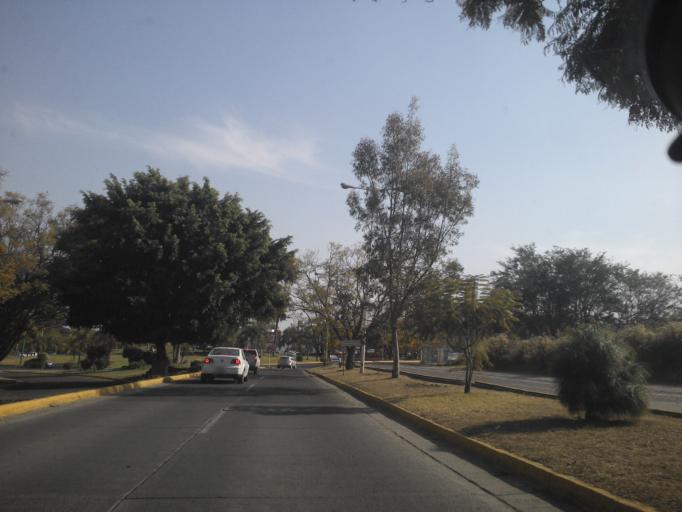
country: MX
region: Jalisco
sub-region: Tlajomulco de Zuniga
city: Palomar
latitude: 20.6032
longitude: -103.4475
